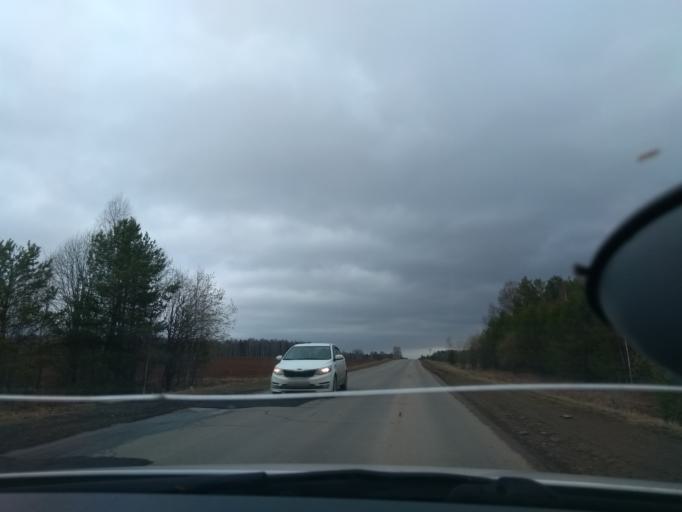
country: RU
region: Perm
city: Orda
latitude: 57.3451
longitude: 56.7898
